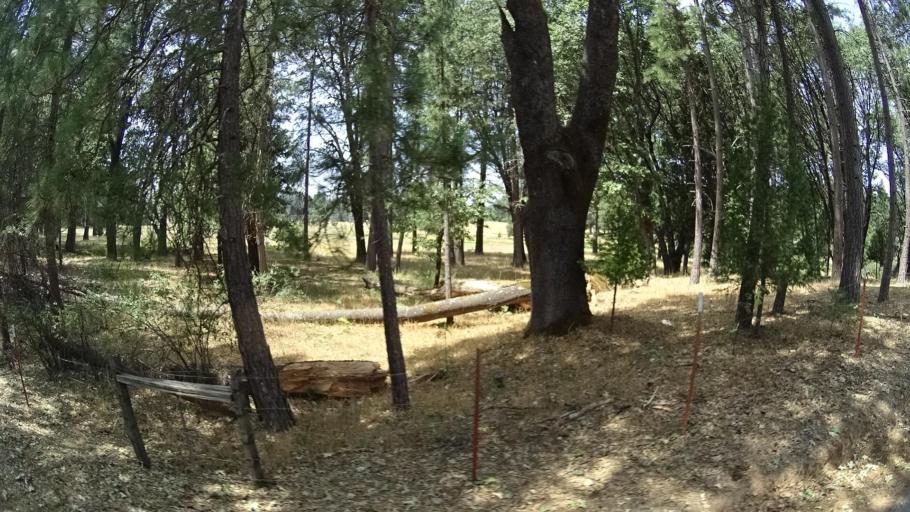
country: US
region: California
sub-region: Mariposa County
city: Midpines
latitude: 37.7239
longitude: -120.0901
